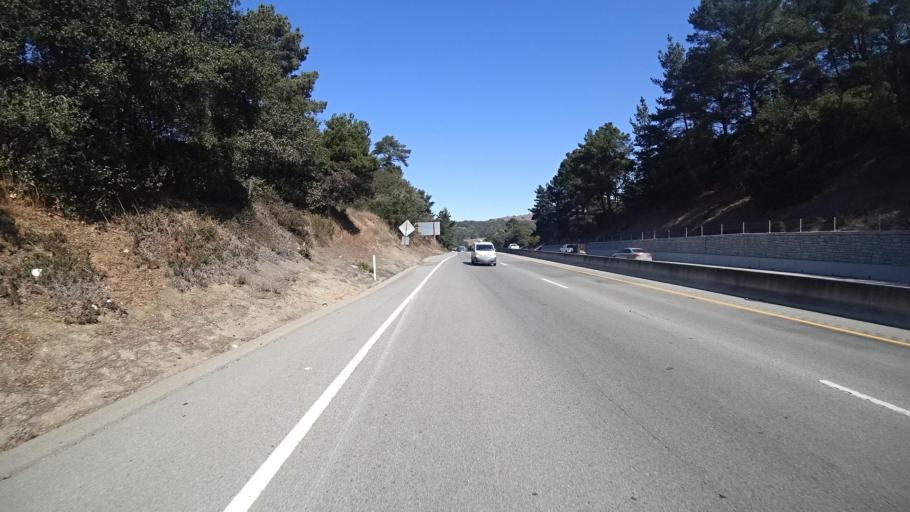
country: US
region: California
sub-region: Monterey County
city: Prunedale
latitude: 36.8231
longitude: -121.6308
